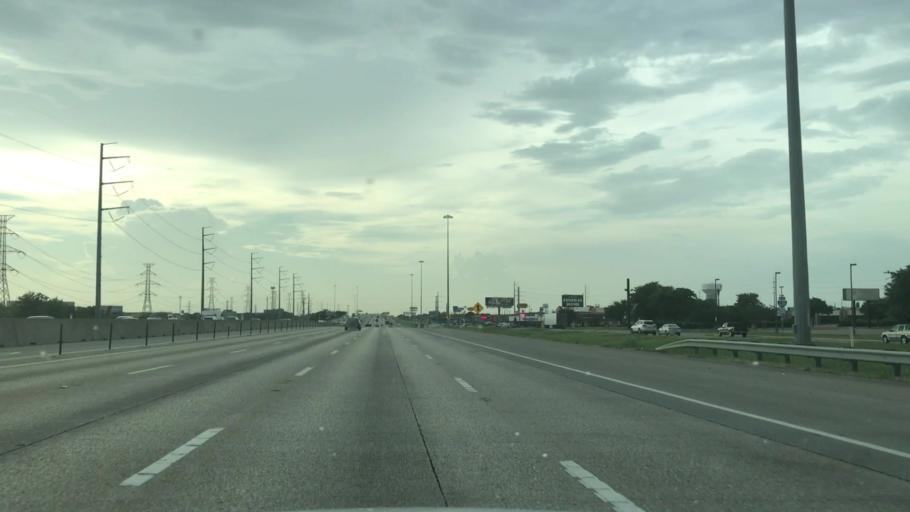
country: US
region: Texas
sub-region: Dallas County
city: Garland
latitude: 32.8599
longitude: -96.6546
